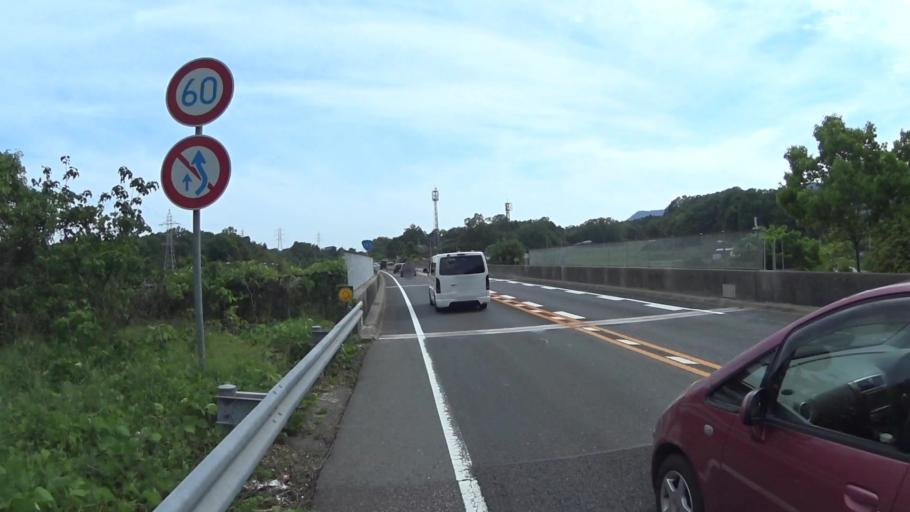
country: JP
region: Shiga Prefecture
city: Kitahama
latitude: 35.0985
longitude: 135.8913
